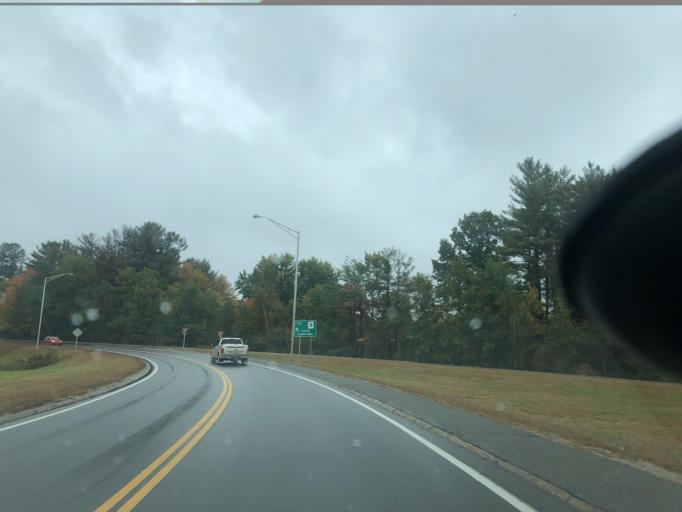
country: US
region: New Hampshire
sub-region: Strafford County
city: Dover
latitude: 43.1857
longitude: -70.8859
